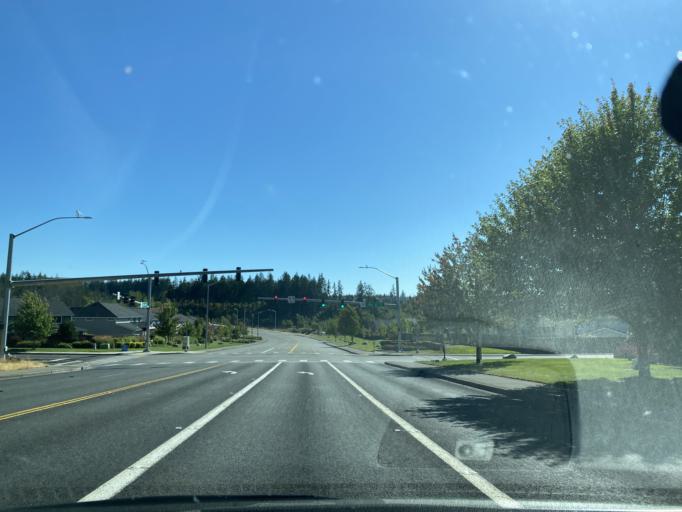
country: US
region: Washington
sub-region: Pierce County
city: Graham
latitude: 47.0918
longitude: -122.2676
